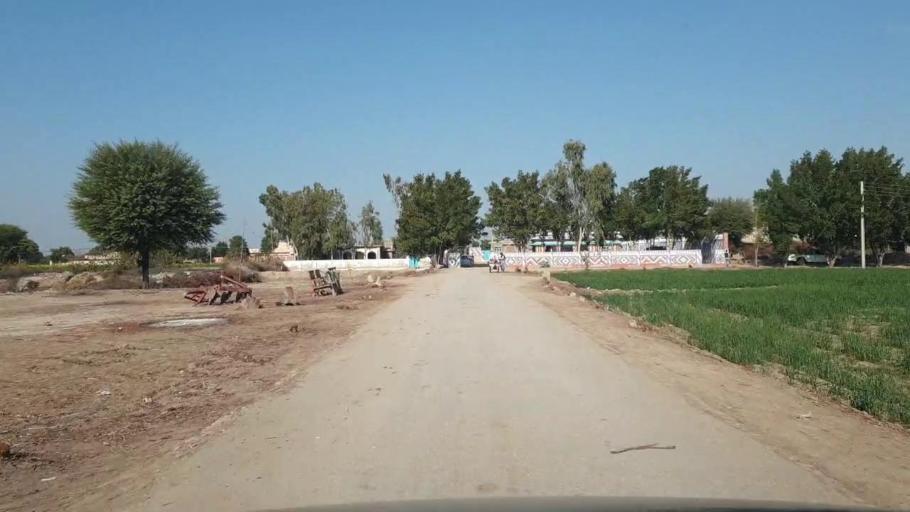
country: PK
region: Sindh
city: Shahpur Chakar
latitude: 26.1549
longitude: 68.6649
